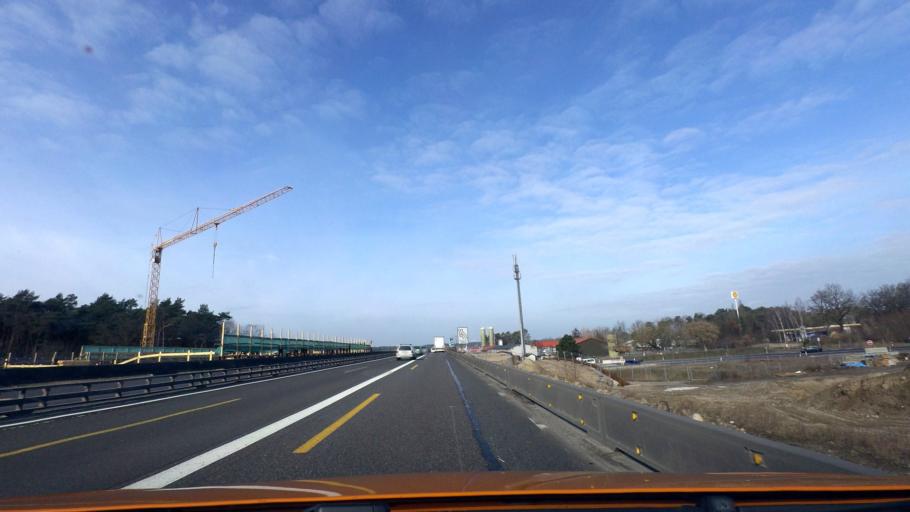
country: DE
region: Brandenburg
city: Michendorf
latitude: 52.3000
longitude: 13.0271
